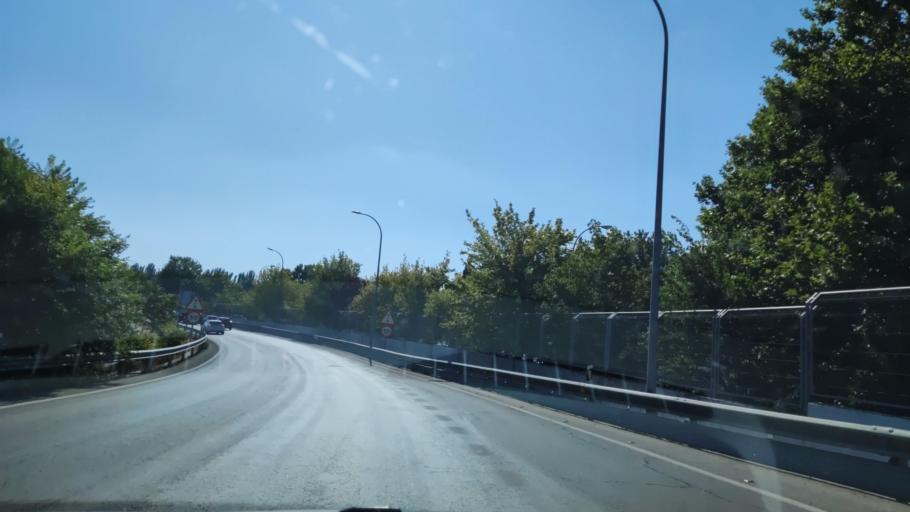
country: ES
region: Madrid
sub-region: Provincia de Madrid
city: Alcorcon
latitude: 40.3592
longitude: -3.8089
